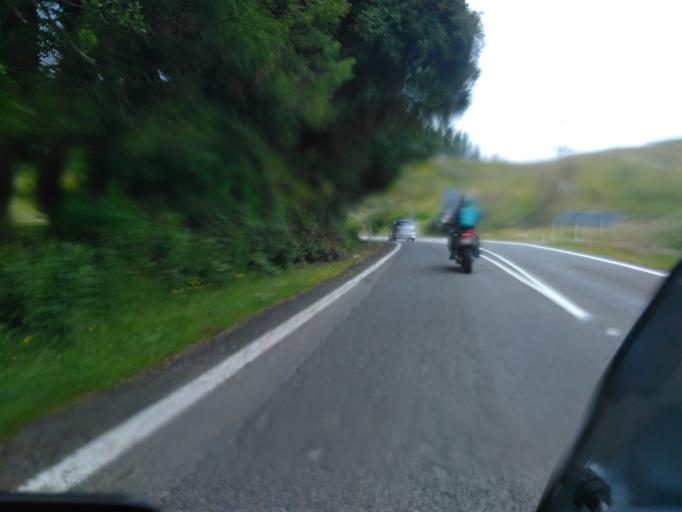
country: NZ
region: Bay of Plenty
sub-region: Opotiki District
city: Opotiki
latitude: -38.3587
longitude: 177.5378
